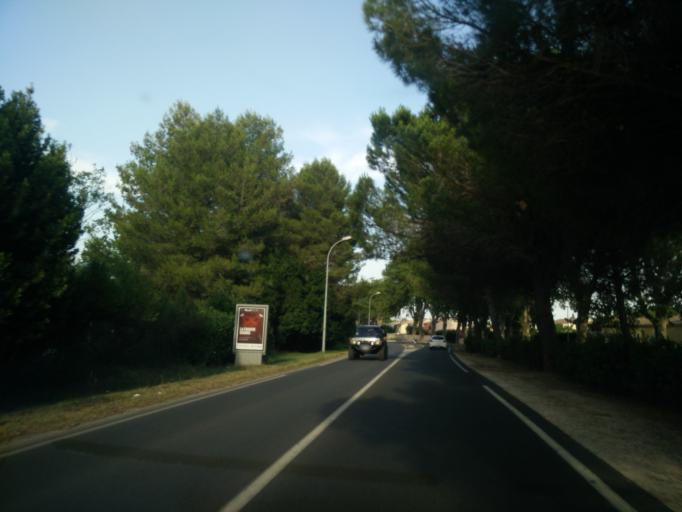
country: FR
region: Languedoc-Roussillon
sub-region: Departement de l'Herault
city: Marsillargues
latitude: 43.6633
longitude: 4.1659
